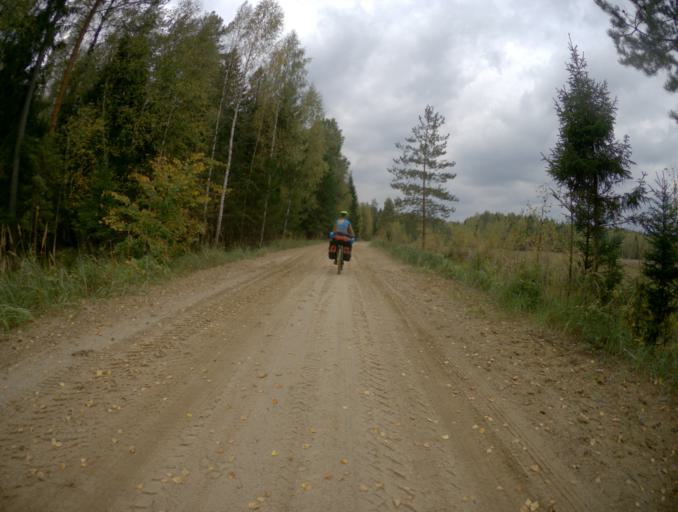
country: RU
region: Vladimir
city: Kideksha
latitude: 56.4704
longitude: 40.6870
